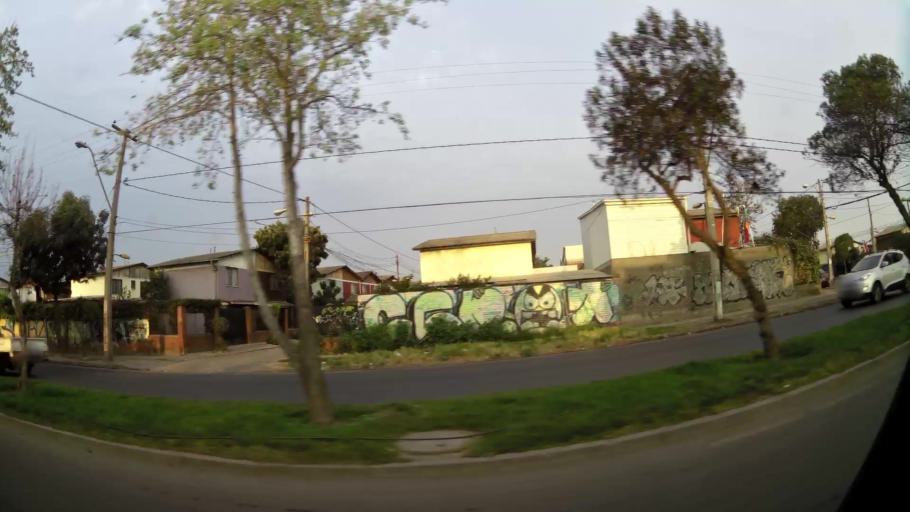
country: CL
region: Santiago Metropolitan
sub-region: Provincia de Santiago
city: Lo Prado
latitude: -33.5077
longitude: -70.7903
